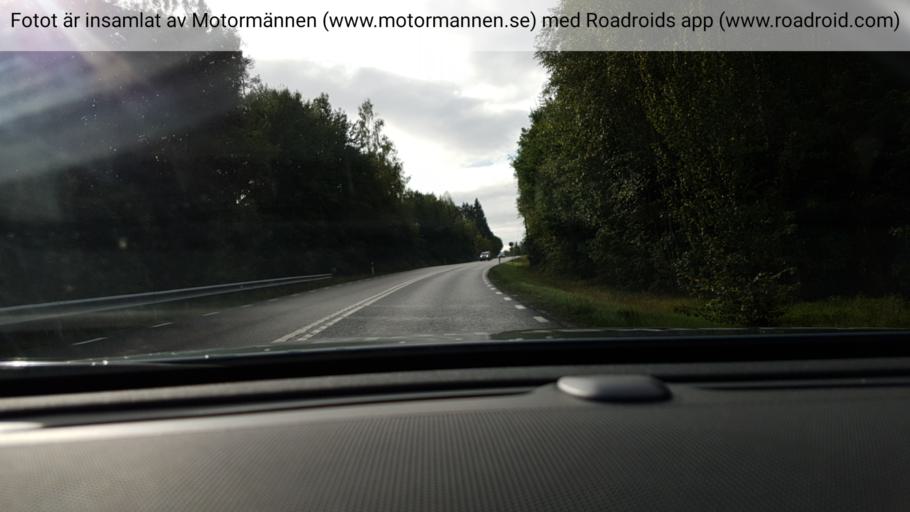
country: SE
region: Vaestra Goetaland
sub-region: Harryda Kommun
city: Ravlanda
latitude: 57.5756
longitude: 12.5053
